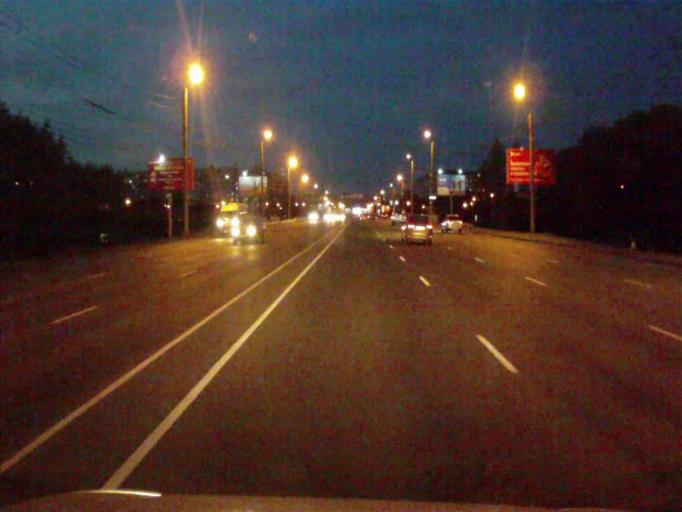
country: RU
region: Chelyabinsk
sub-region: Gorod Chelyabinsk
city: Chelyabinsk
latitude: 55.1726
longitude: 61.3582
